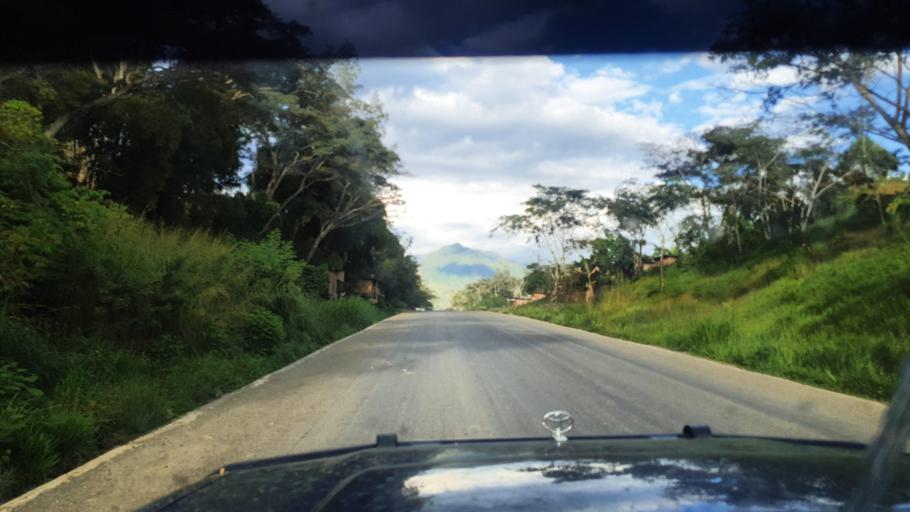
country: PG
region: Chimbu
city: Kundiawa
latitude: -5.9429
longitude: 144.8444
